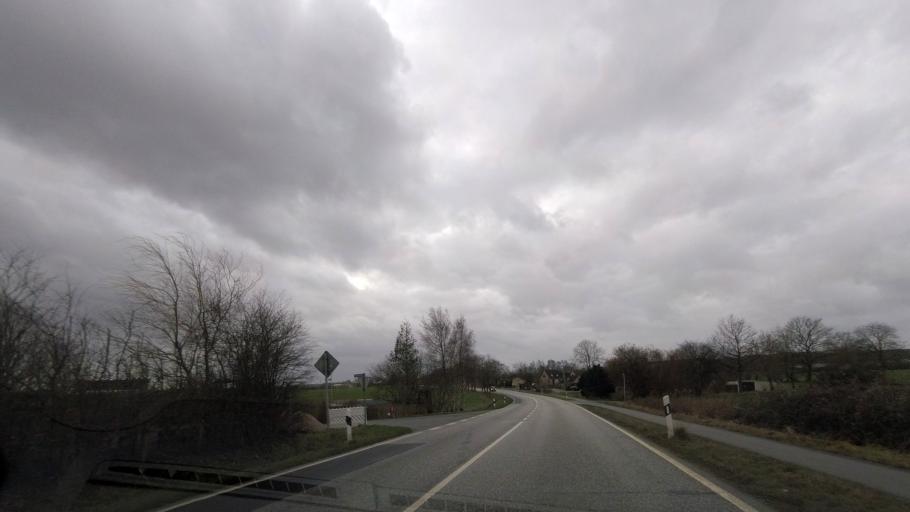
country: DE
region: Schleswig-Holstein
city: Twedt
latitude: 54.5928
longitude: 9.6703
